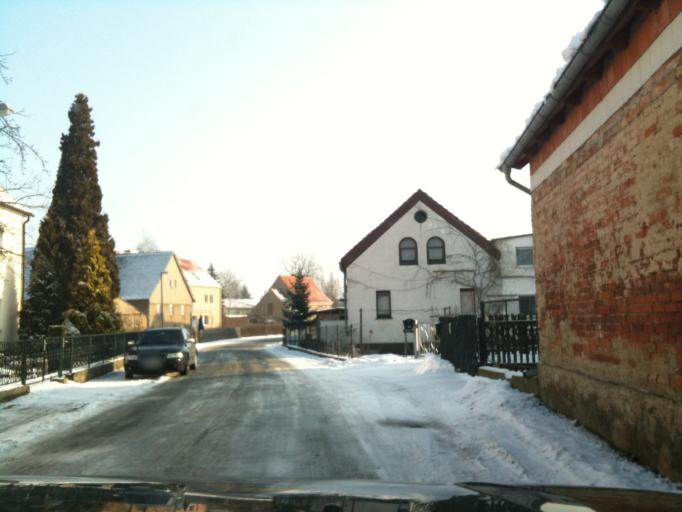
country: DE
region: Saxony
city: Goerlitz
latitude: 51.1185
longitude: 14.9824
